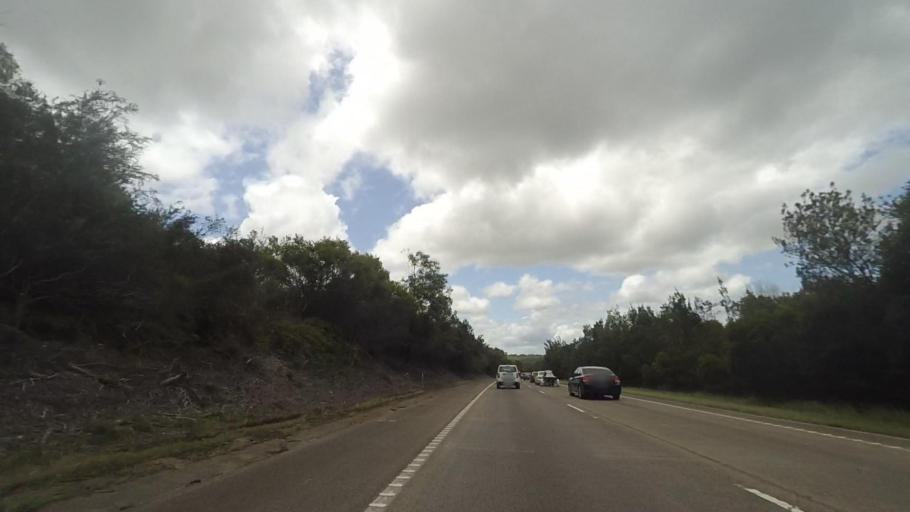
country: AU
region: New South Wales
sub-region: Gosford Shire
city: Narara
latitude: -33.3946
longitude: 151.2970
